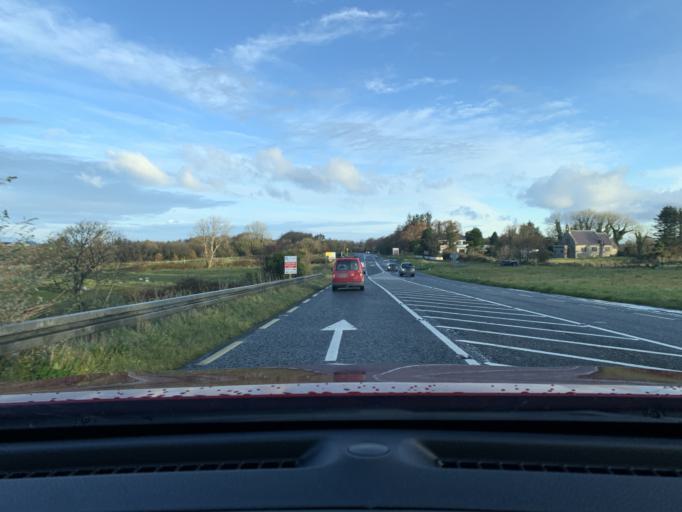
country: IE
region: Connaught
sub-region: Sligo
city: Strandhill
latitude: 54.3715
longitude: -8.5308
